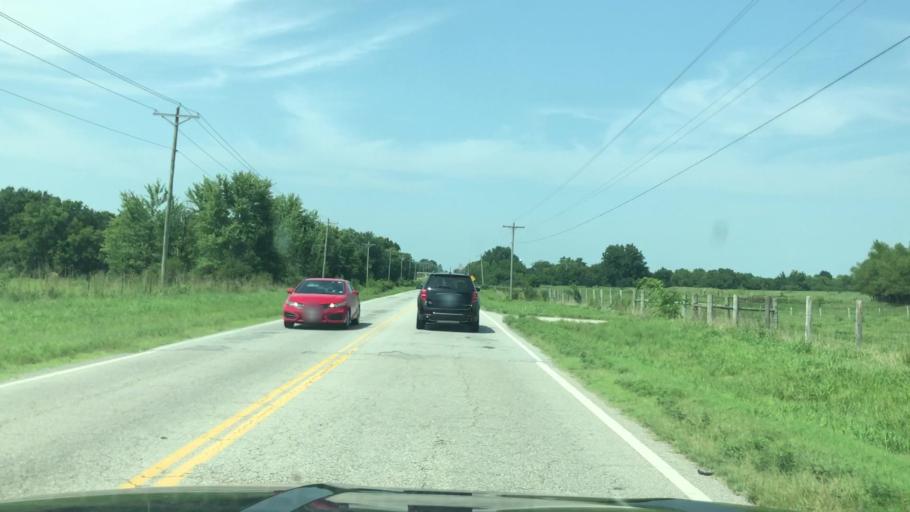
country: US
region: Oklahoma
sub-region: Ottawa County
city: Miami
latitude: 36.8935
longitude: -94.8418
